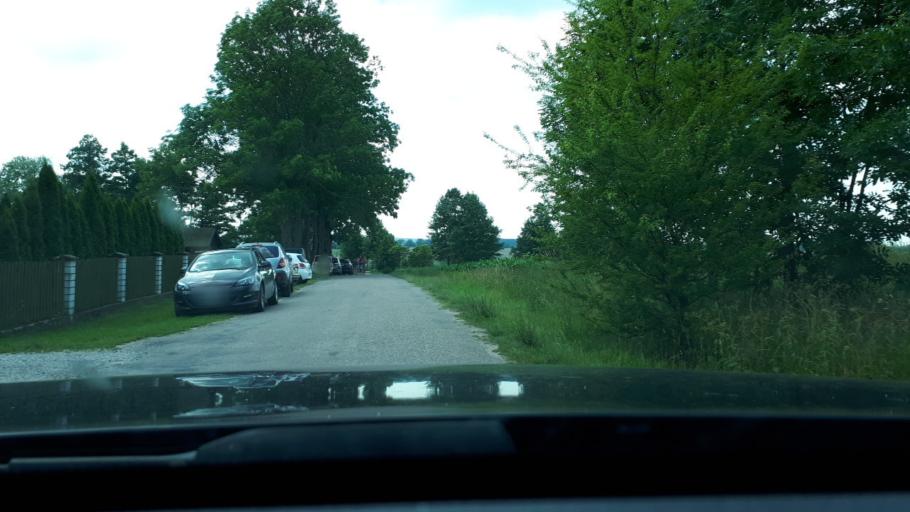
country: PL
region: Podlasie
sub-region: Powiat bialostocki
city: Lapy
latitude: 53.0849
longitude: 22.8324
